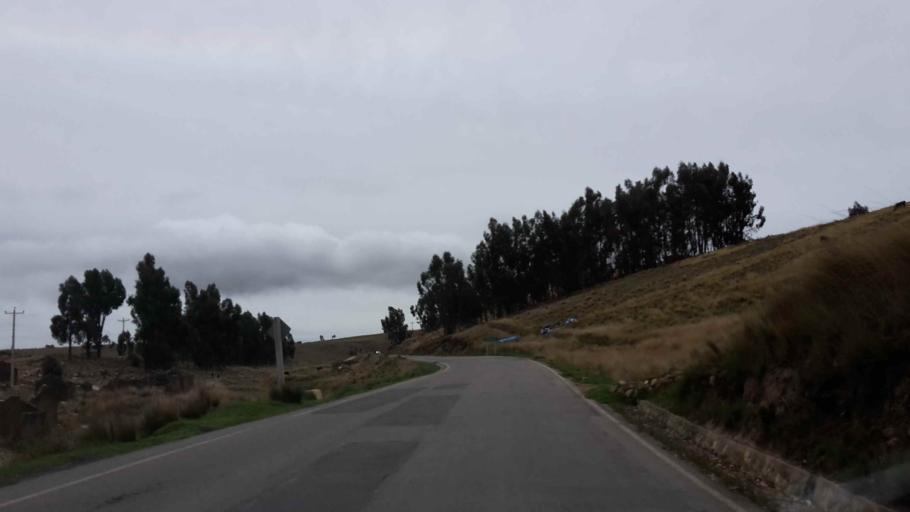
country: BO
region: Cochabamba
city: Arani
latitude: -17.4867
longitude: -65.6089
